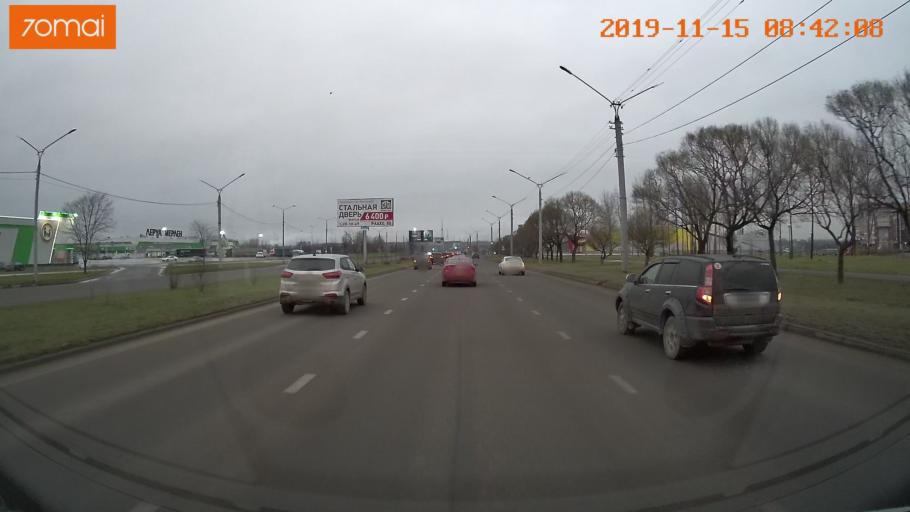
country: RU
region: Vologda
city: Cherepovets
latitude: 59.1007
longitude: 37.9095
